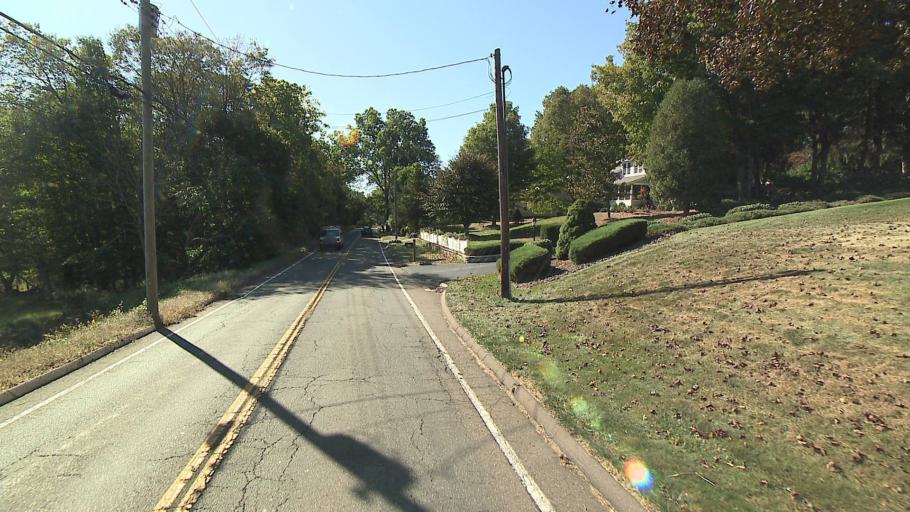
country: US
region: Connecticut
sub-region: New Haven County
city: Orange
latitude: 41.3068
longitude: -73.0192
